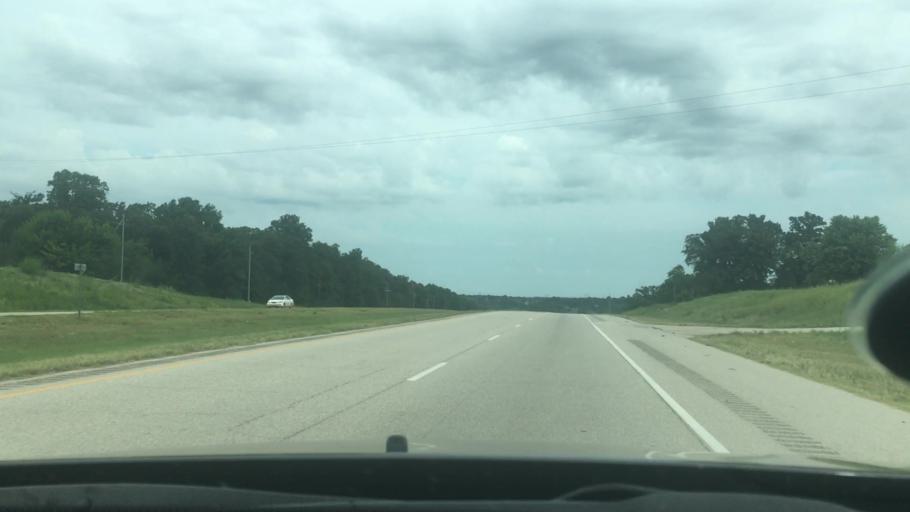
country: US
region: Oklahoma
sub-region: Pontotoc County
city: Byng
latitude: 34.9163
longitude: -96.6809
